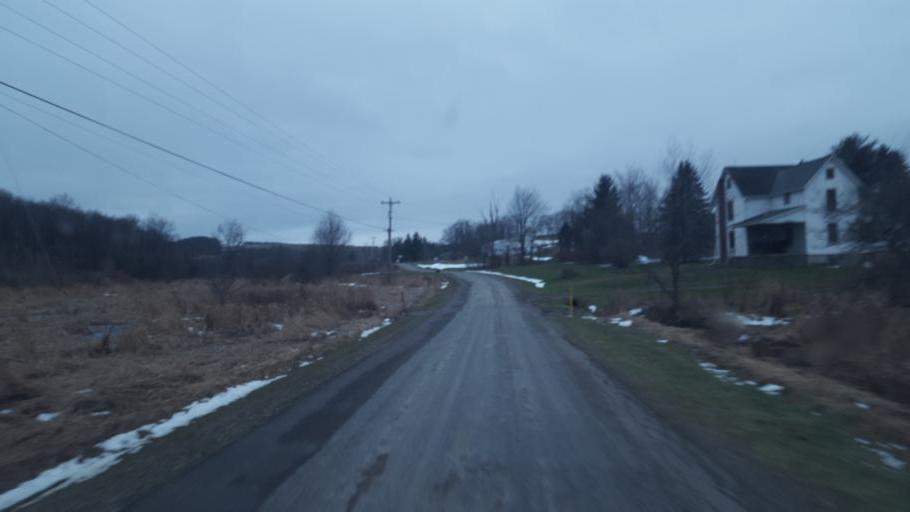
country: US
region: Pennsylvania
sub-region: Potter County
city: Galeton
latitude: 41.8895
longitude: -77.8078
